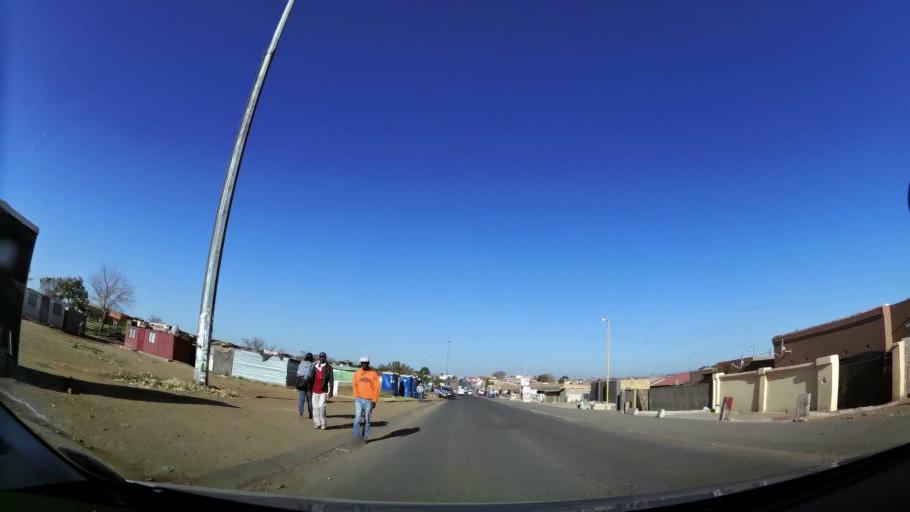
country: ZA
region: Gauteng
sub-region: Ekurhuleni Metropolitan Municipality
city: Tembisa
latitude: -26.0116
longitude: 28.2223
